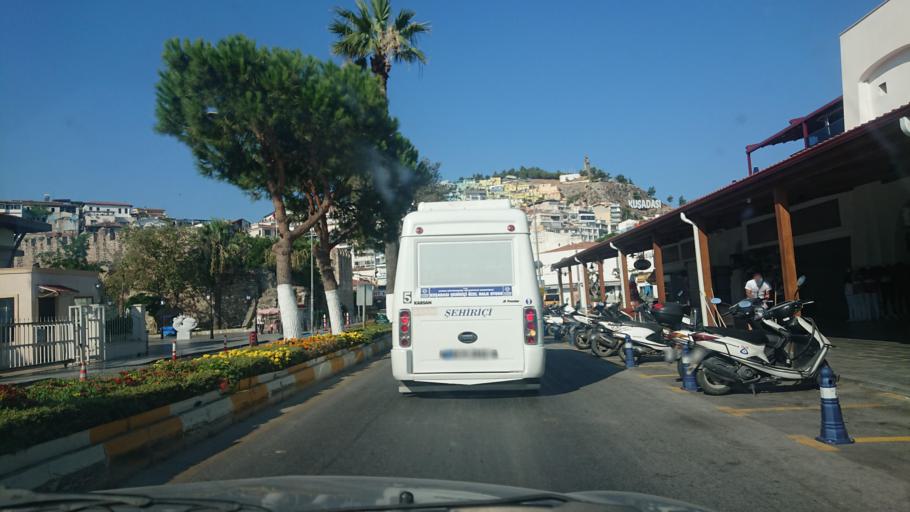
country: TR
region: Aydin
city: Kusadasi
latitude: 37.8610
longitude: 27.2572
